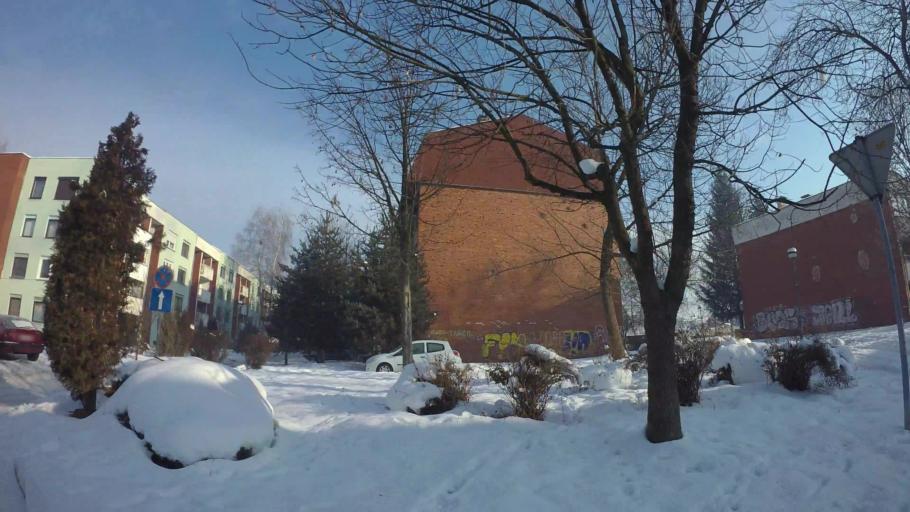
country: BA
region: Federation of Bosnia and Herzegovina
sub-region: Kanton Sarajevo
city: Sarajevo
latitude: 43.8232
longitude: 18.3530
